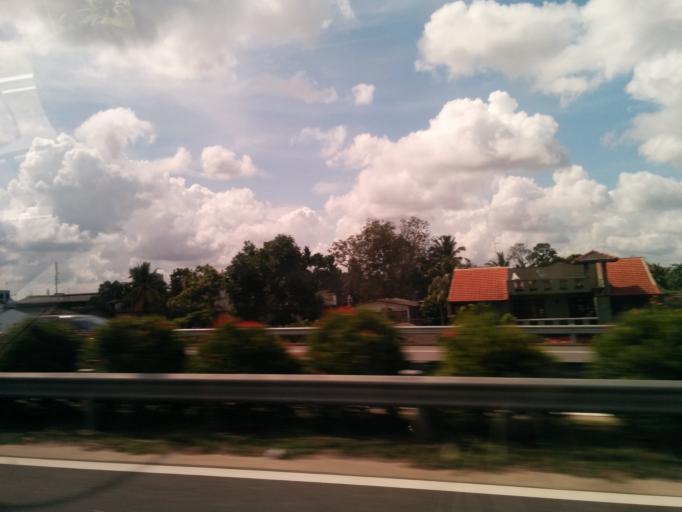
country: LK
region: Western
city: Peliyagoda
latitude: 6.9583
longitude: 79.8852
